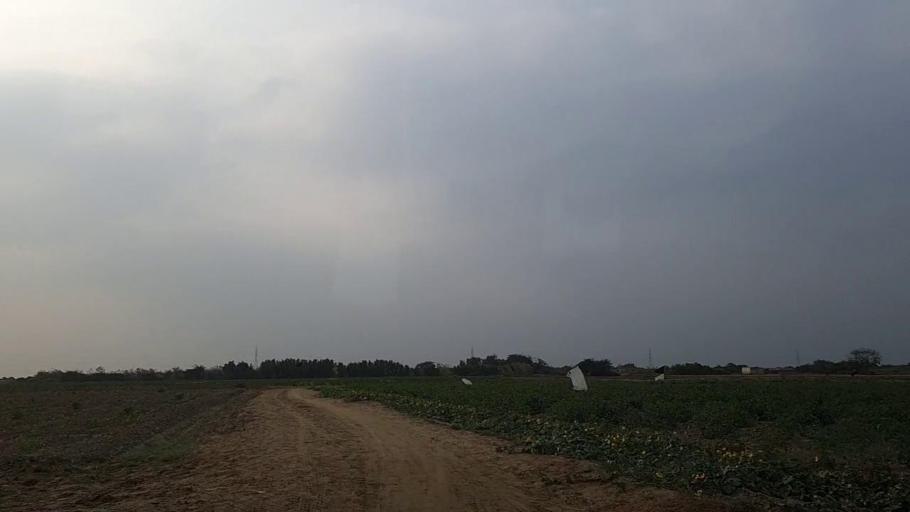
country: PK
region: Sindh
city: Mirpur Sakro
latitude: 24.6171
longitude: 67.5047
